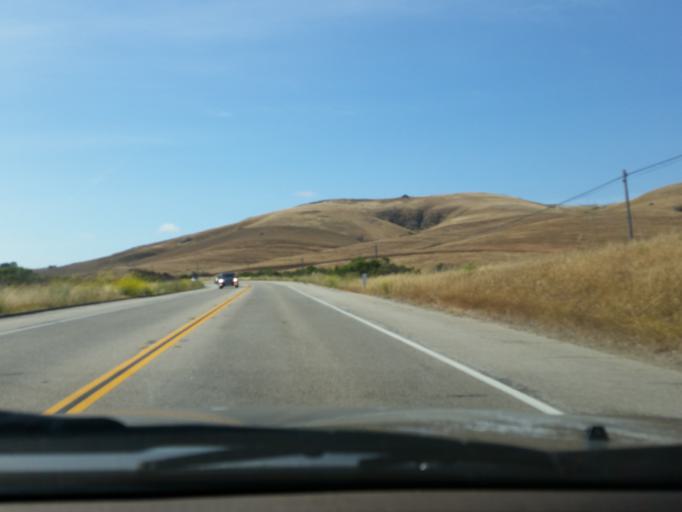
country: US
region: California
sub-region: San Luis Obispo County
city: Cambria
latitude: 35.4924
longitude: -121.0034
